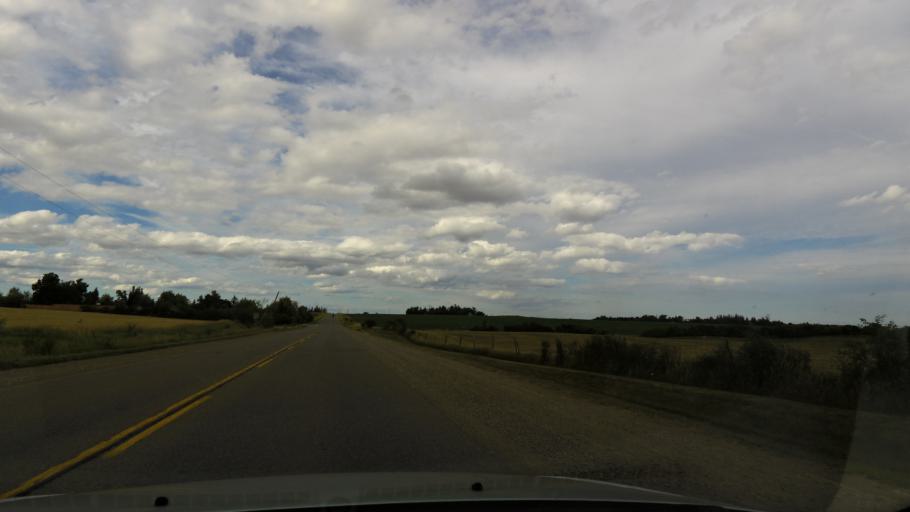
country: CA
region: Ontario
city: Brampton
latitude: 43.6687
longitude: -79.8958
